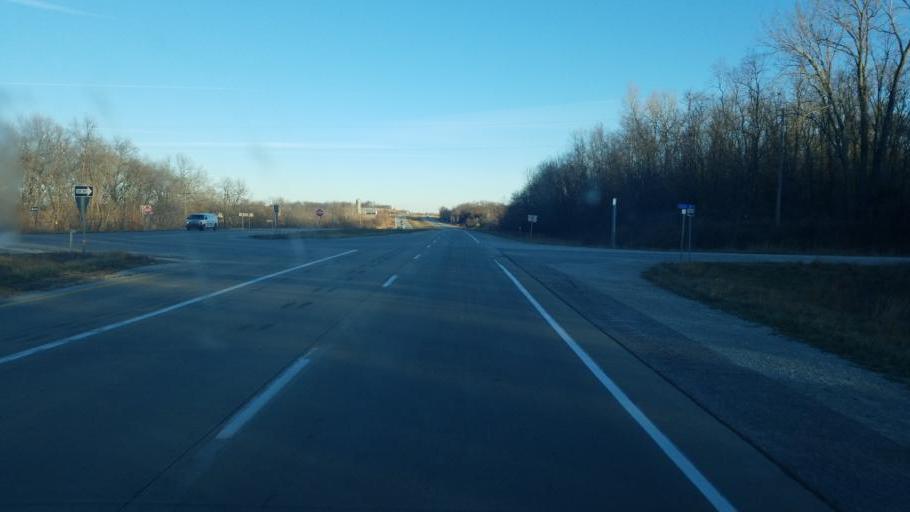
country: US
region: Iowa
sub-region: Wapello County
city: Eddyville
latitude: 41.2046
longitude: -92.6399
